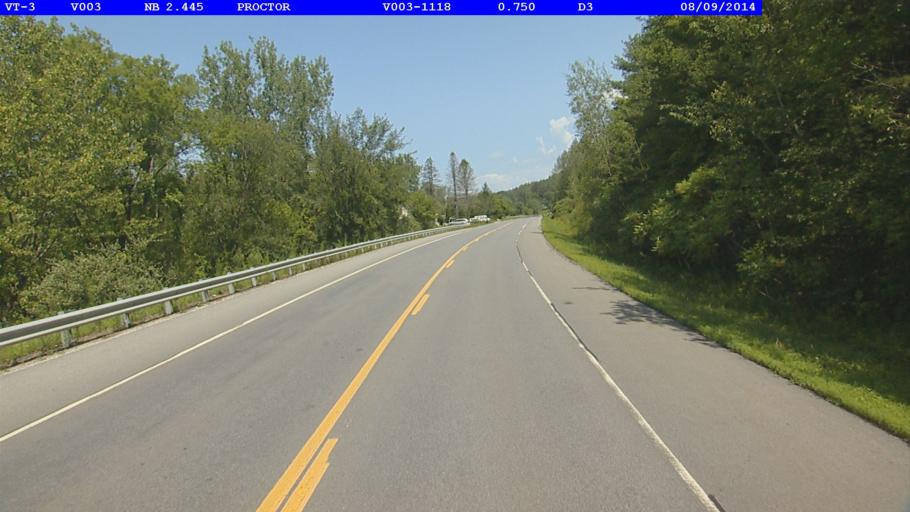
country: US
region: Vermont
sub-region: Rutland County
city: West Rutland
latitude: 43.6349
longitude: -73.0348
